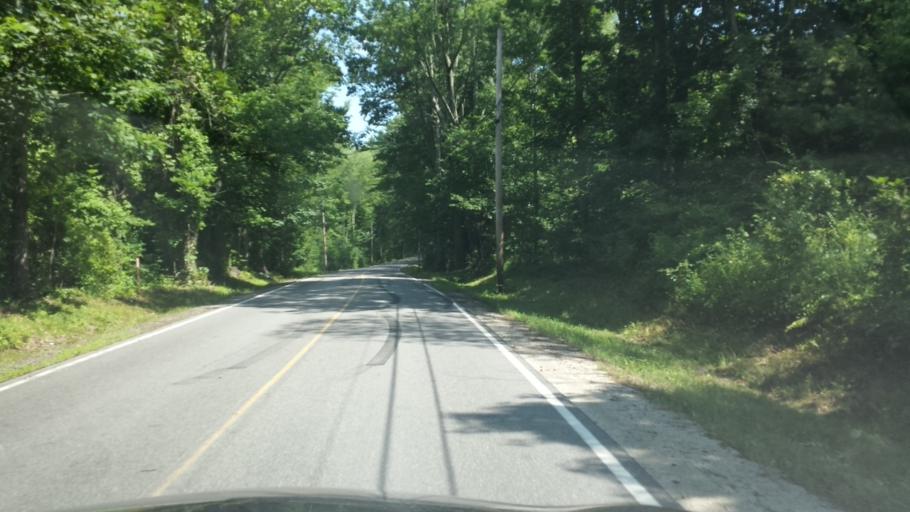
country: US
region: Maine
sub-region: York County
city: Kennebunk
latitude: 43.4476
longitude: -70.5183
